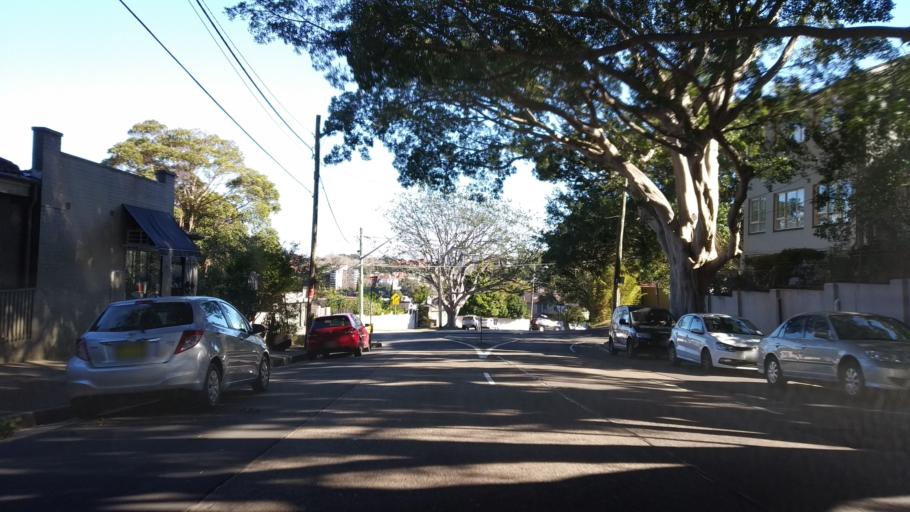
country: AU
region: New South Wales
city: Edgecliff
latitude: -33.8822
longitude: 151.2518
